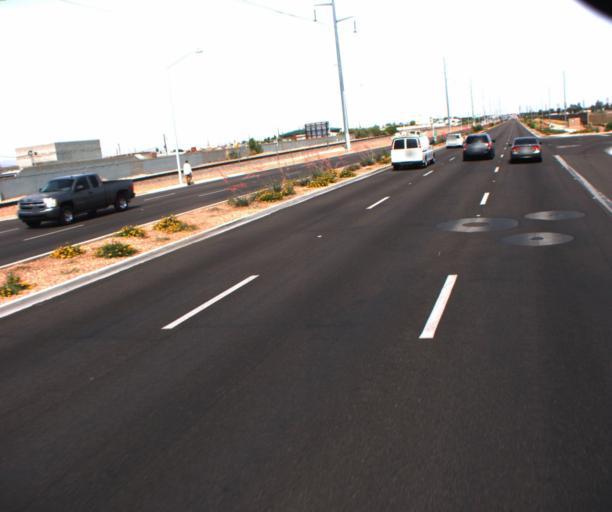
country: US
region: Arizona
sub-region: Maricopa County
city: Glendale
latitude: 33.5459
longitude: -112.1946
